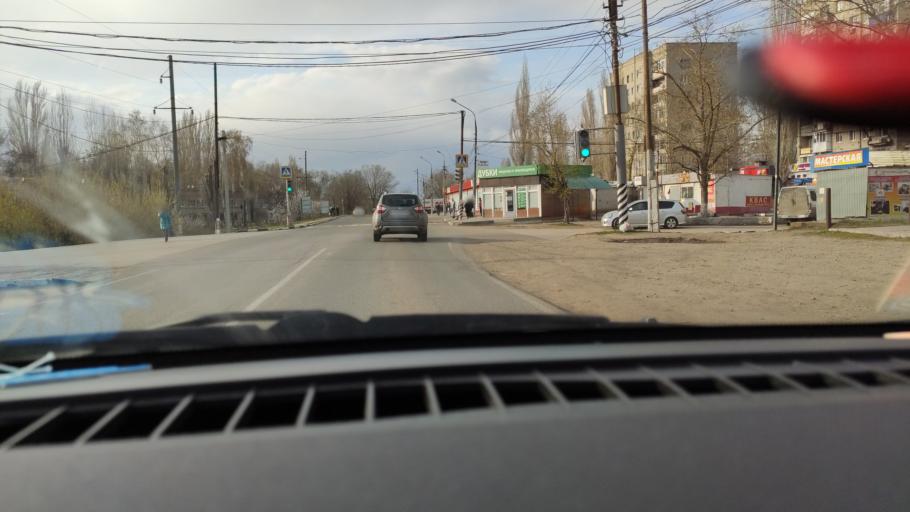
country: RU
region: Saratov
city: Privolzhskiy
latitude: 51.3926
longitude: 46.0345
